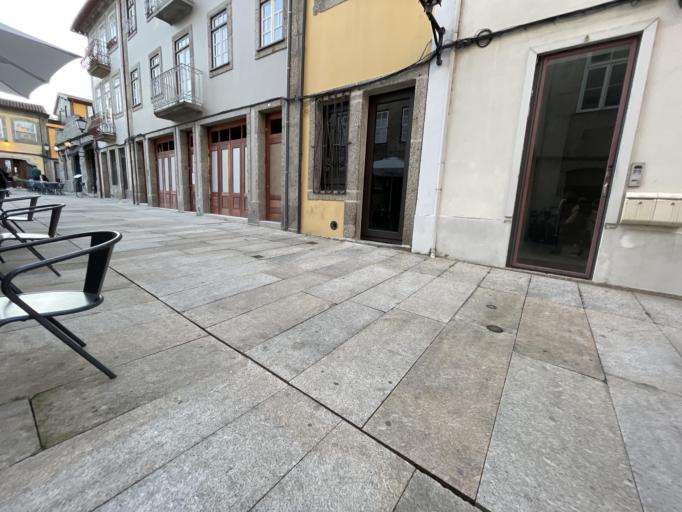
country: PT
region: Braga
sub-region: Guimaraes
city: Guimaraes
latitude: 41.4425
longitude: -8.2926
